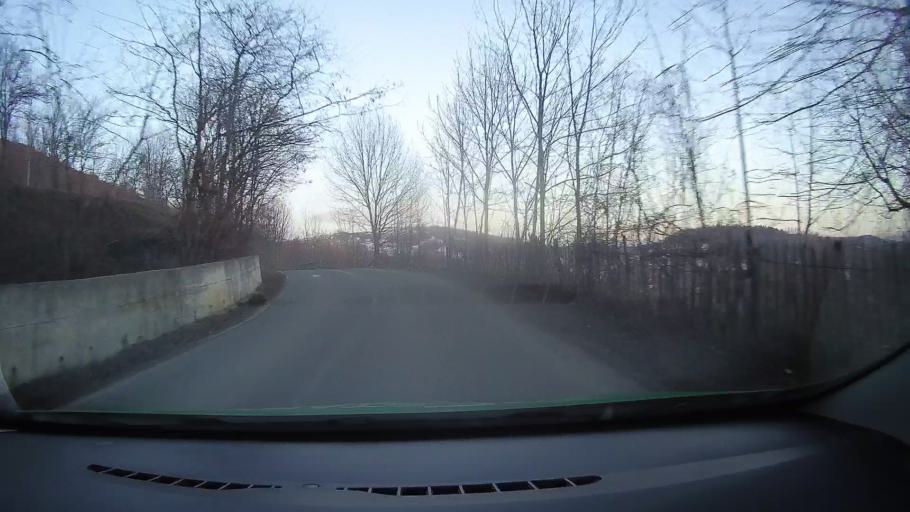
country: RO
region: Prahova
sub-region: Comuna Comarnic
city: Poiana
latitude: 45.2597
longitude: 25.6541
